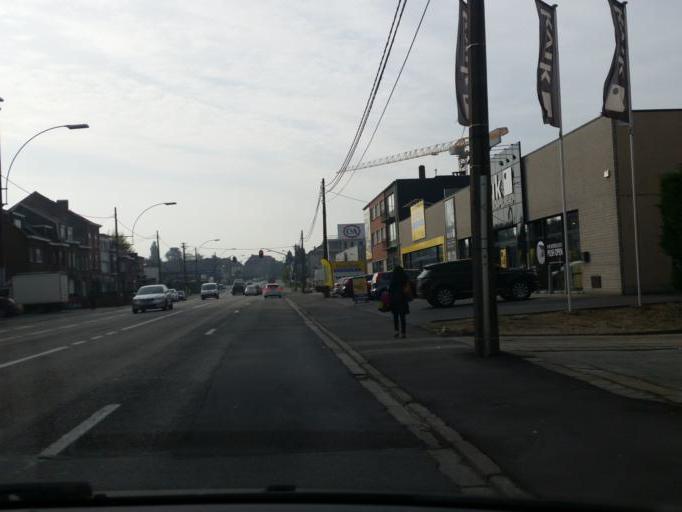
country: BE
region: Flanders
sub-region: Provincie Vlaams-Brabant
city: Drogenbos
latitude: 50.8034
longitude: 4.2886
